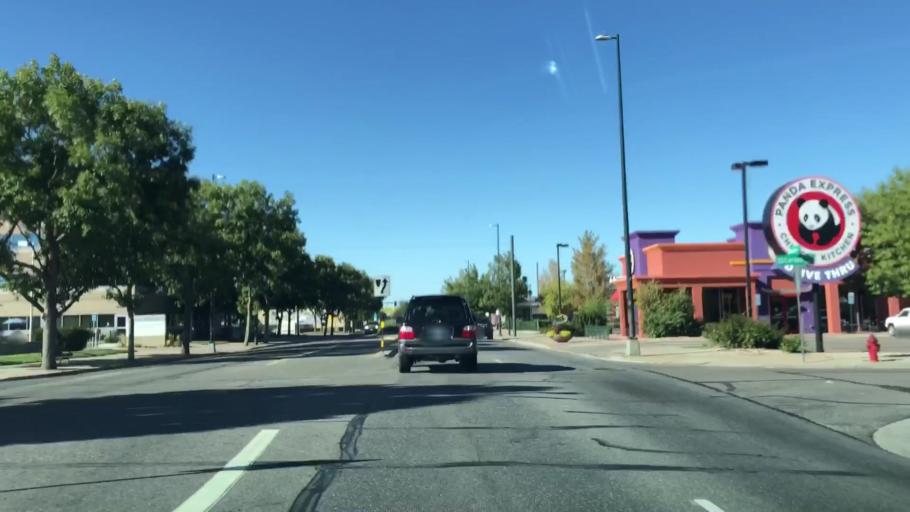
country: US
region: Colorado
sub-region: Arapahoe County
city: Englewood
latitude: 39.6621
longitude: -104.9876
